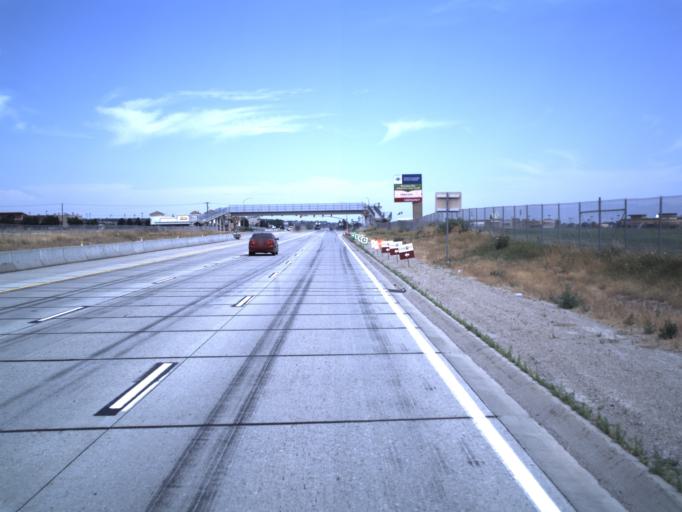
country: US
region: Utah
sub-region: Salt Lake County
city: Riverton
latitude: 40.5189
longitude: -111.9840
